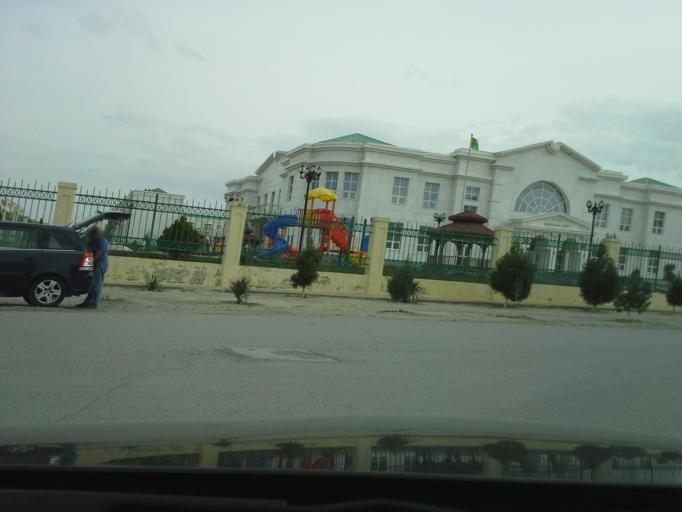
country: TM
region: Ahal
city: Abadan
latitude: 38.0538
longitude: 58.1404
